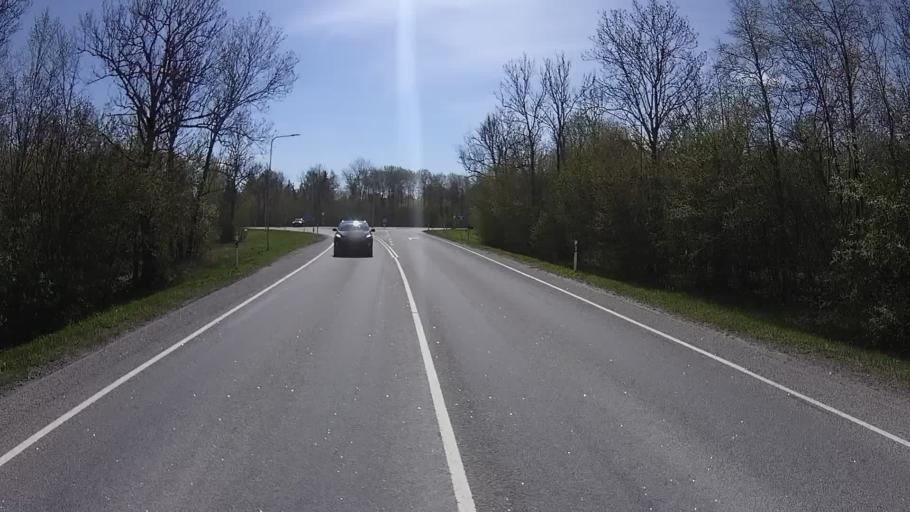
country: EE
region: Laeaene
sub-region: Ridala Parish
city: Uuemoisa
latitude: 58.9588
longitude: 23.6681
